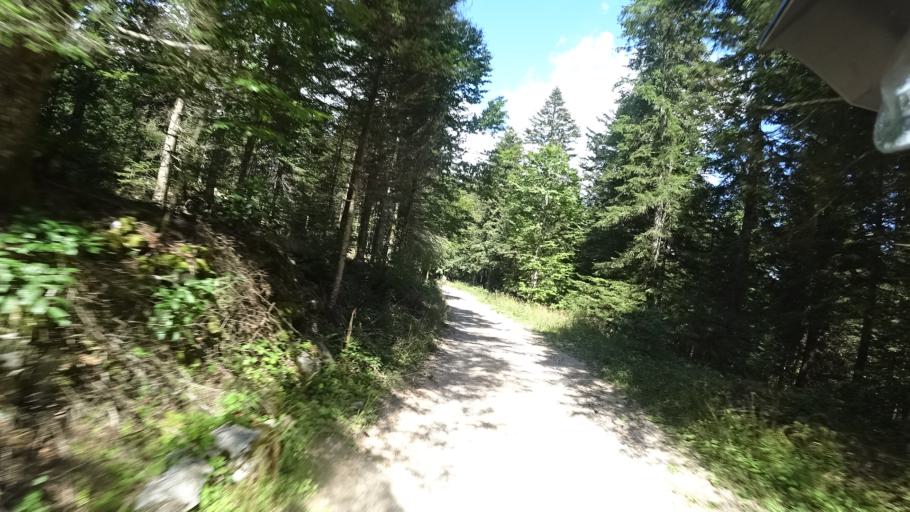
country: BA
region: Federation of Bosnia and Herzegovina
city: Orasac
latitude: 44.5054
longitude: 15.9280
